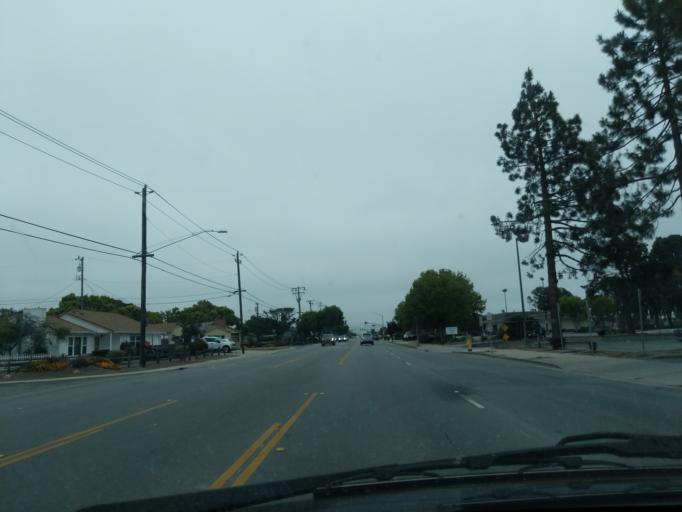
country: US
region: California
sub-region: Monterey County
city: Salinas
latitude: 36.6987
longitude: -121.6491
